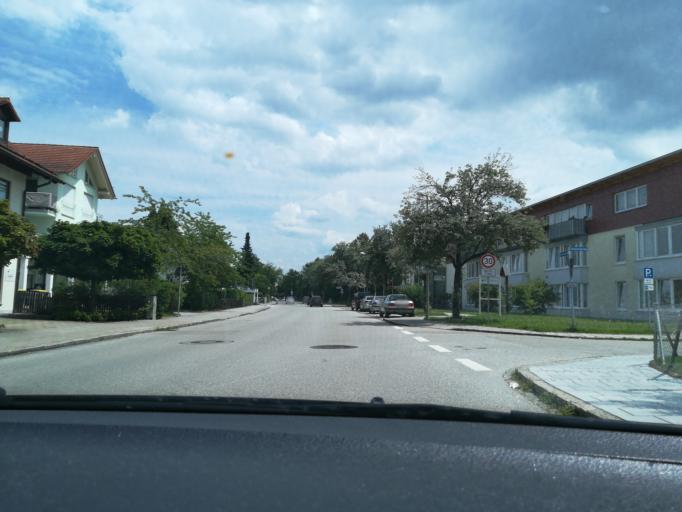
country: DE
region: Bavaria
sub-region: Upper Bavaria
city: Hohenkirchen-Siegertsbrunn
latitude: 48.0193
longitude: 11.7140
